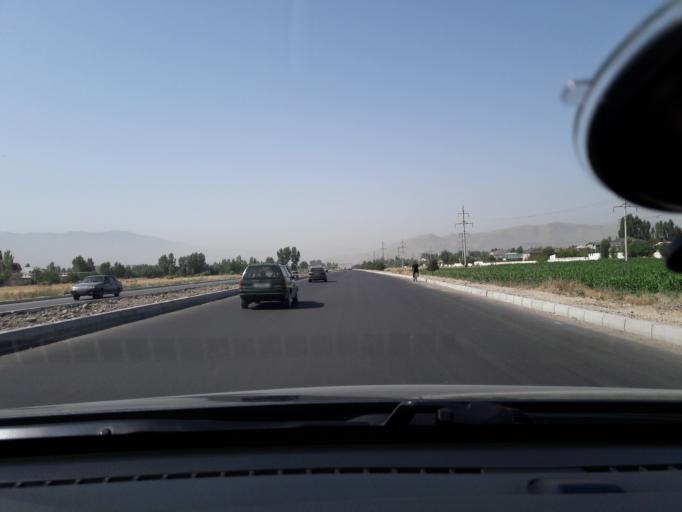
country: TJ
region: Dushanbe
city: Dushanbe
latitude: 38.4913
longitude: 68.7517
